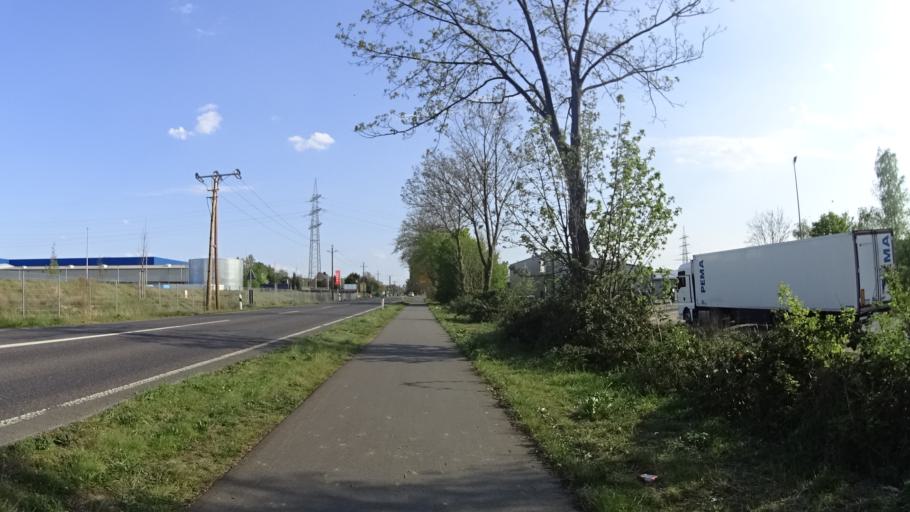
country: DE
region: North Rhine-Westphalia
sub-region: Regierungsbezirk Dusseldorf
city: Dormagen
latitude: 51.1300
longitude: 6.8051
